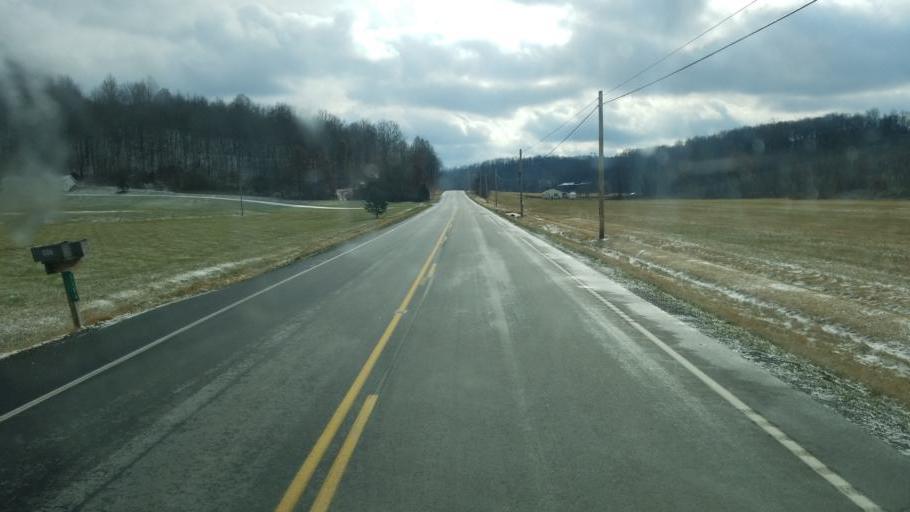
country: US
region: Ohio
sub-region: Muskingum County
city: Frazeysburg
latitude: 40.1303
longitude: -82.1970
